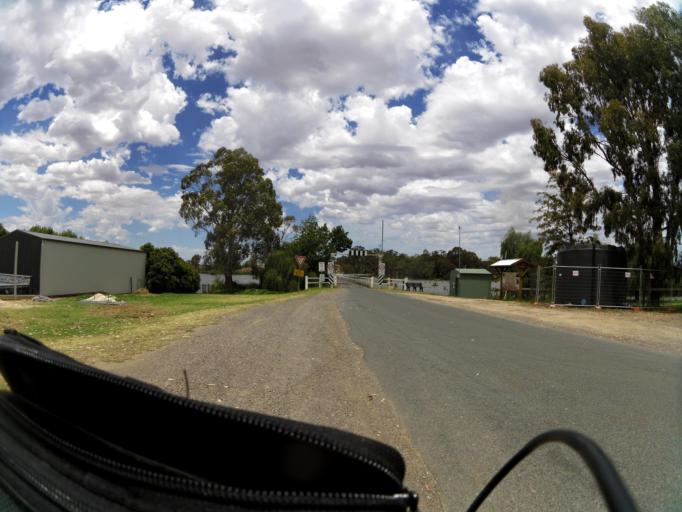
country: AU
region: Victoria
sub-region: Campaspe
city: Kyabram
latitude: -36.7444
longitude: 145.1383
